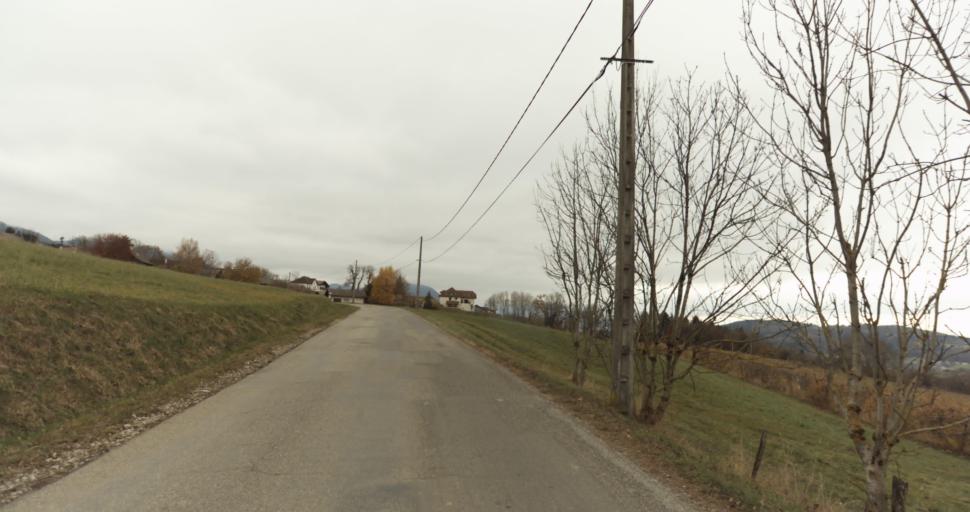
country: FR
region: Rhone-Alpes
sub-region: Departement de la Haute-Savoie
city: Saint-Martin-Bellevue
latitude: 45.9813
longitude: 6.1815
